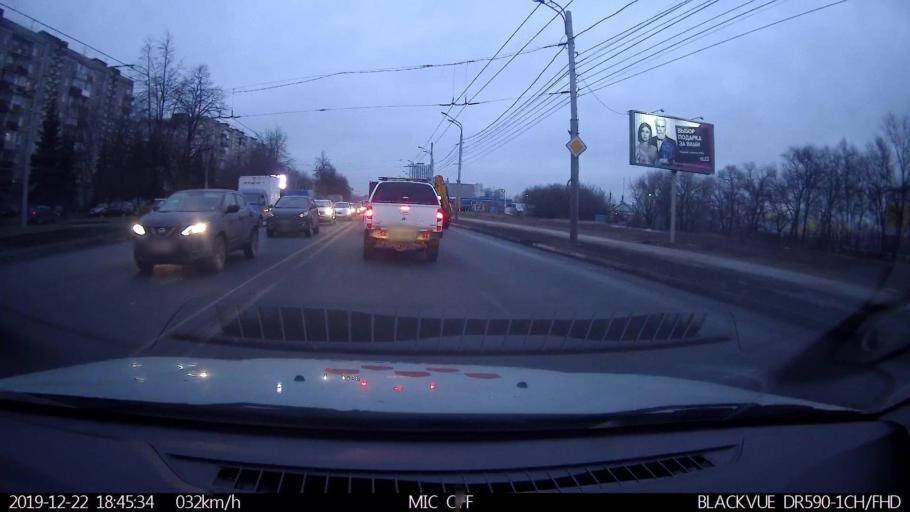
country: RU
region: Nizjnij Novgorod
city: Nizhniy Novgorod
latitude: 56.3391
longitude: 43.8820
